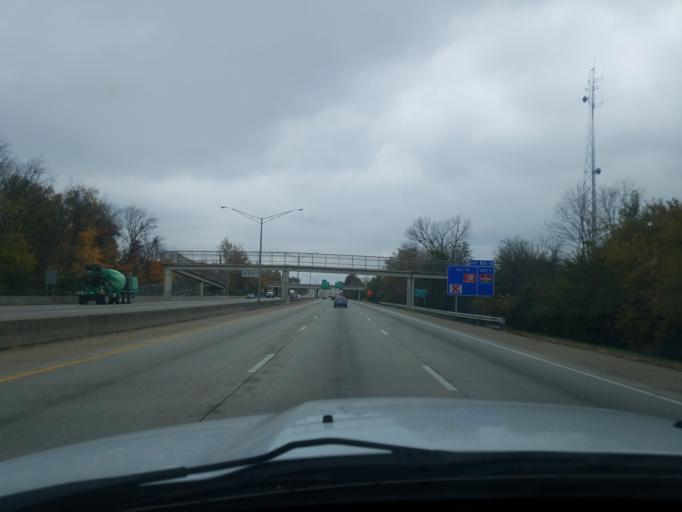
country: US
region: Kentucky
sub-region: Jefferson County
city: Shively
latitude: 38.1866
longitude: -85.7975
